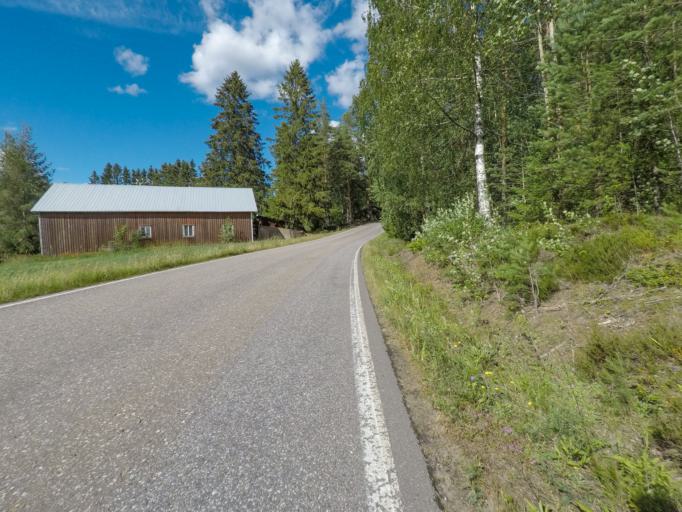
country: FI
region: South Karelia
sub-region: Lappeenranta
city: Joutseno
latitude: 61.1110
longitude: 28.3693
